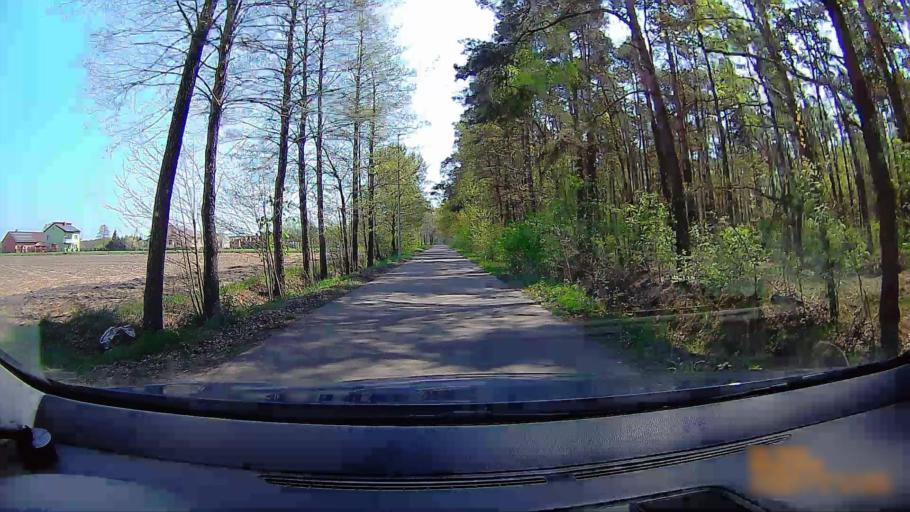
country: PL
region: Greater Poland Voivodeship
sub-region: Powiat koninski
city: Rychwal
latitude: 52.0937
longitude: 18.1715
